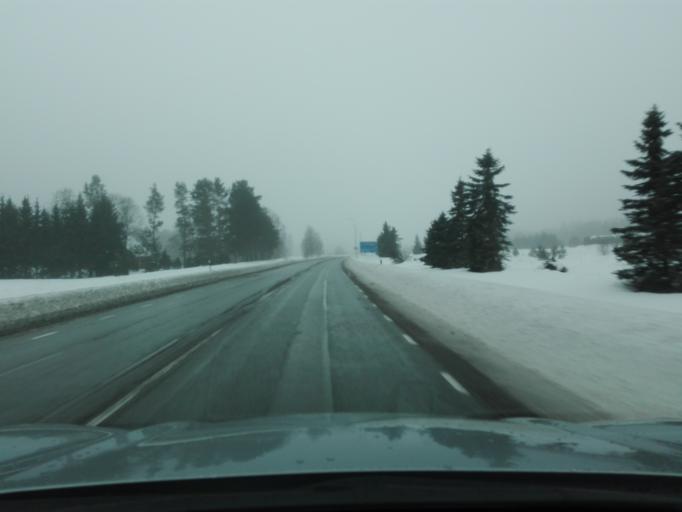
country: EE
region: Harju
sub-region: Kiili vald
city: Kiili
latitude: 59.3278
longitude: 24.7714
